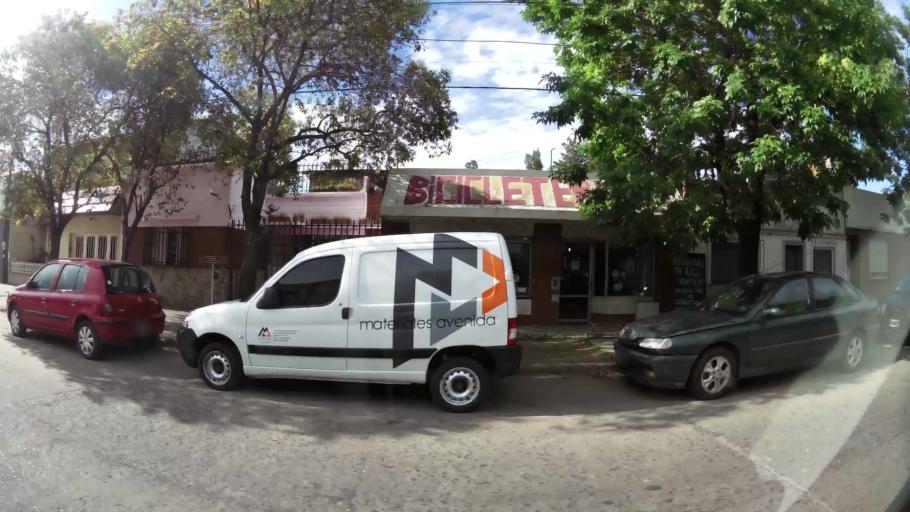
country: AR
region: Santa Fe
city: Granadero Baigorria
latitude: -32.9156
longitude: -60.6968
